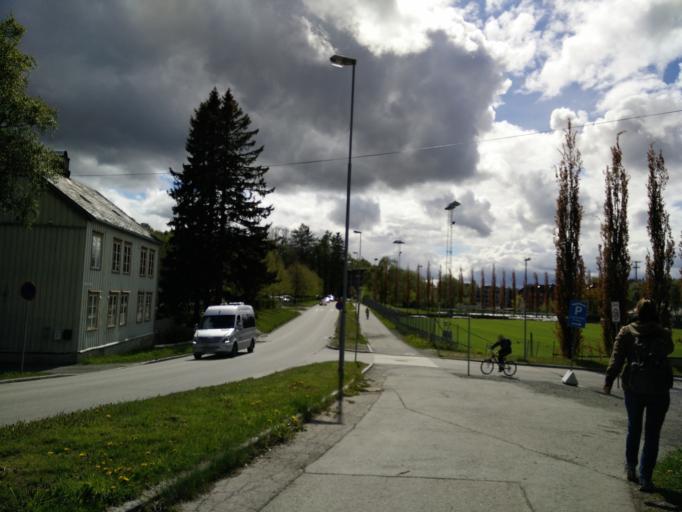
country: NO
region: Sor-Trondelag
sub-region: Trondheim
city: Trondheim
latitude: 63.4119
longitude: 10.4075
